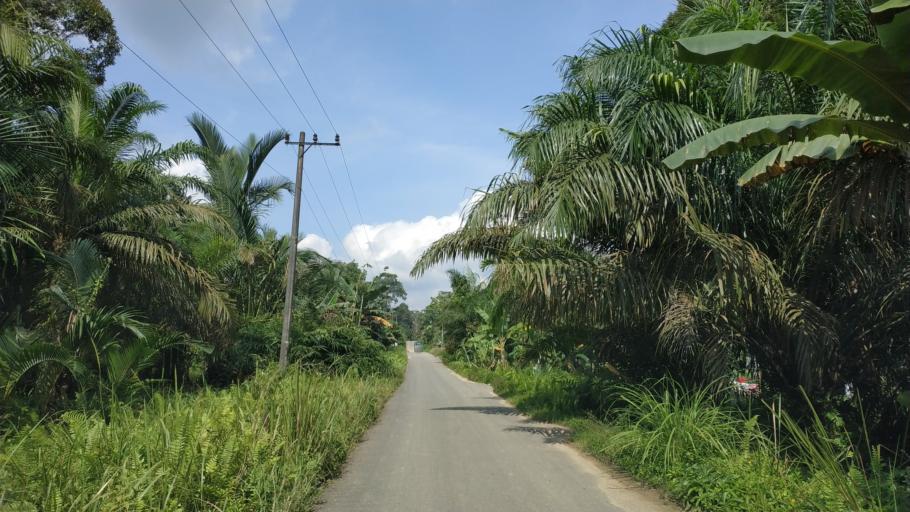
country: ID
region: Riau
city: Pangkalan Kasai
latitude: -0.7263
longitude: 102.4812
